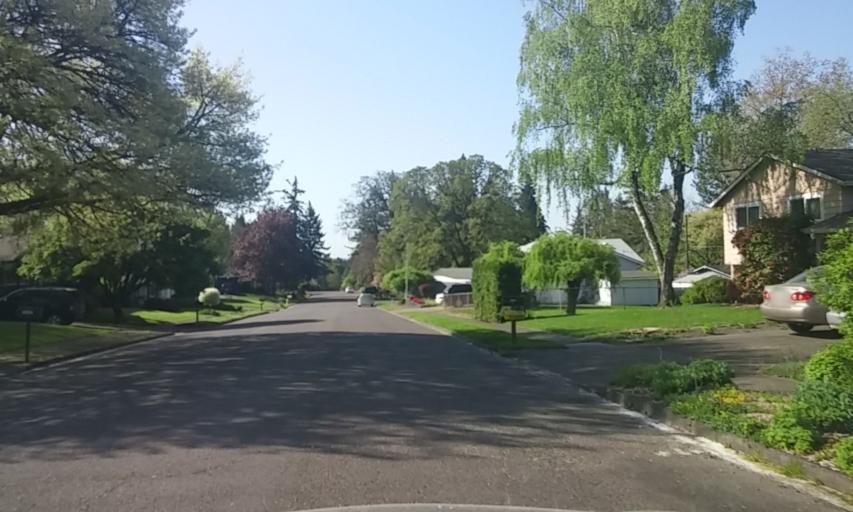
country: US
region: Oregon
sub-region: Washington County
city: Metzger
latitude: 45.4312
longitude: -122.7402
